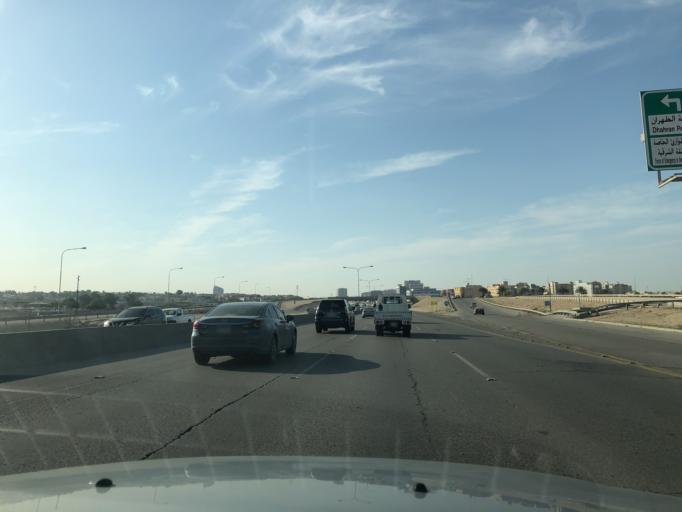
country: SA
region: Eastern Province
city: Dhahran
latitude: 26.3260
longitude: 50.1449
